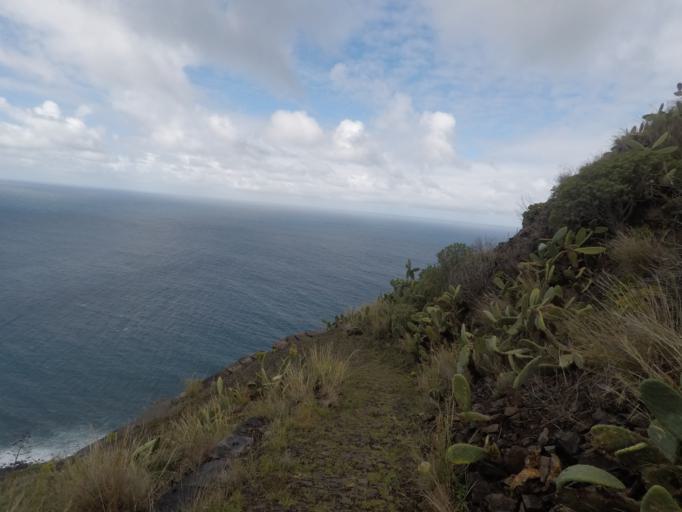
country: PT
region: Madeira
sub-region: Calheta
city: Faja da Ovelha
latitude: 32.7679
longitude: -17.2356
